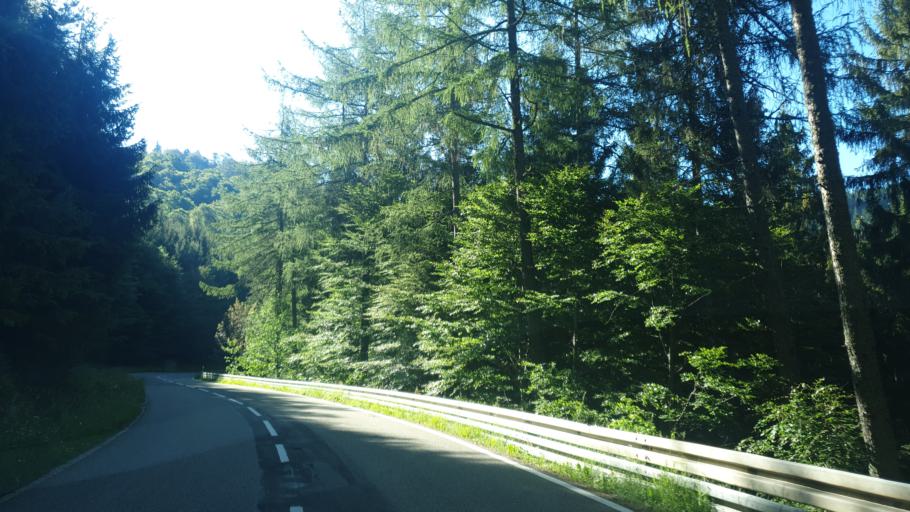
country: DE
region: Baden-Wuerttemberg
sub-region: Freiburg Region
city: Horben
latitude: 47.9110
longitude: 7.8821
